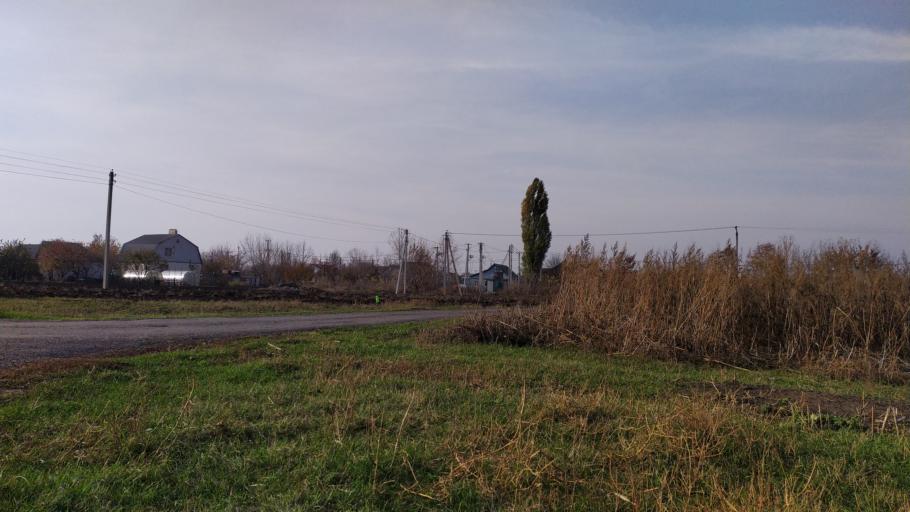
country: RU
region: Kursk
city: Kursk
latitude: 51.6406
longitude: 36.1497
